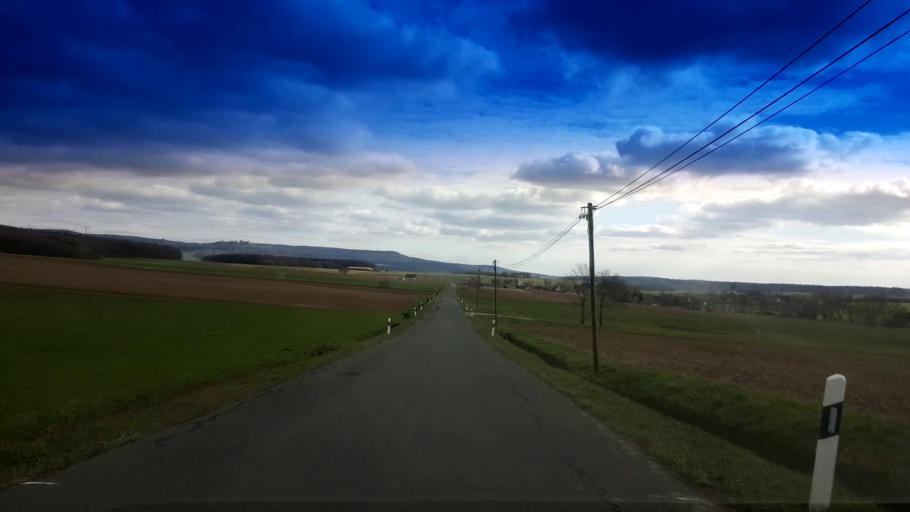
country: DE
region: Bavaria
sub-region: Upper Franconia
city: Schesslitz
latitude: 50.0130
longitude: 11.0199
